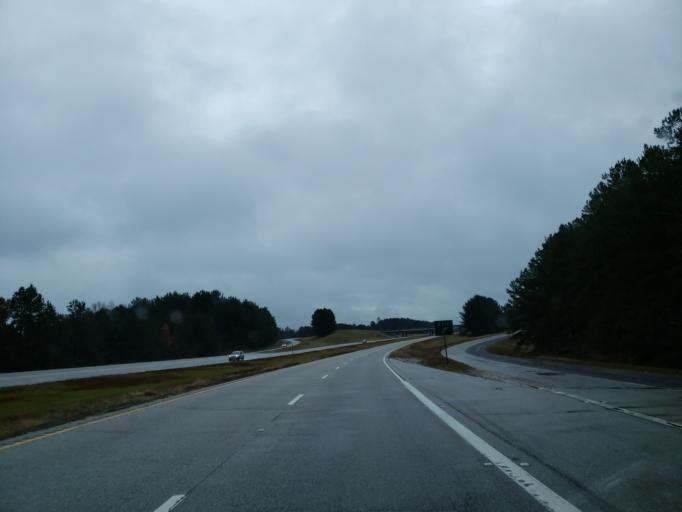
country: US
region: Mississippi
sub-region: Lauderdale County
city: Meridian
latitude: 32.2987
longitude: -88.6937
